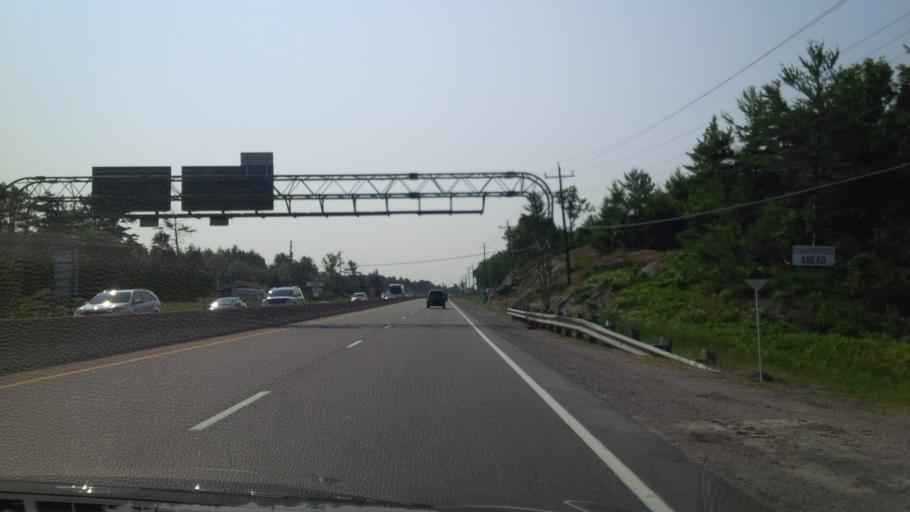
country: CA
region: Ontario
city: Gravenhurst
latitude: 44.8936
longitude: -79.3589
